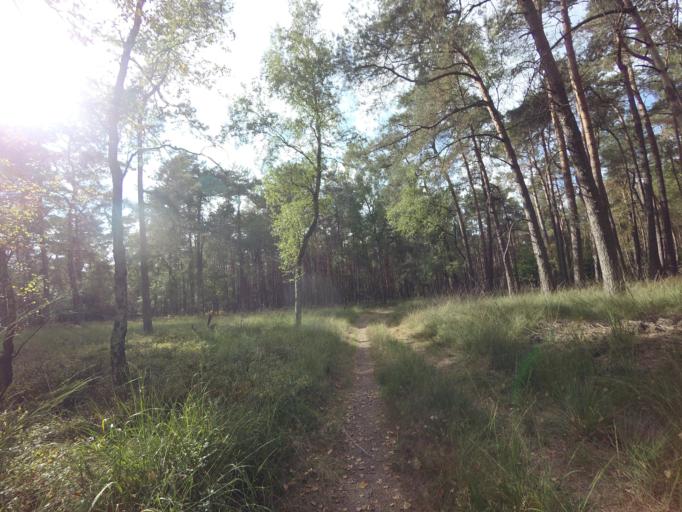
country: NL
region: Gelderland
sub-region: Gemeente Brummen
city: Eerbeek
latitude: 52.0631
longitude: 6.0327
